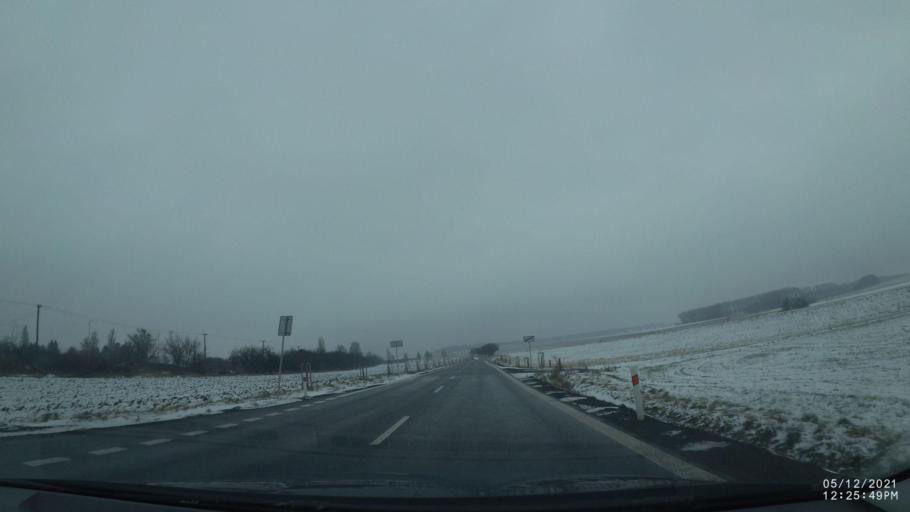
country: CZ
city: Ceske Mezirici
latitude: 50.3253
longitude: 16.0917
